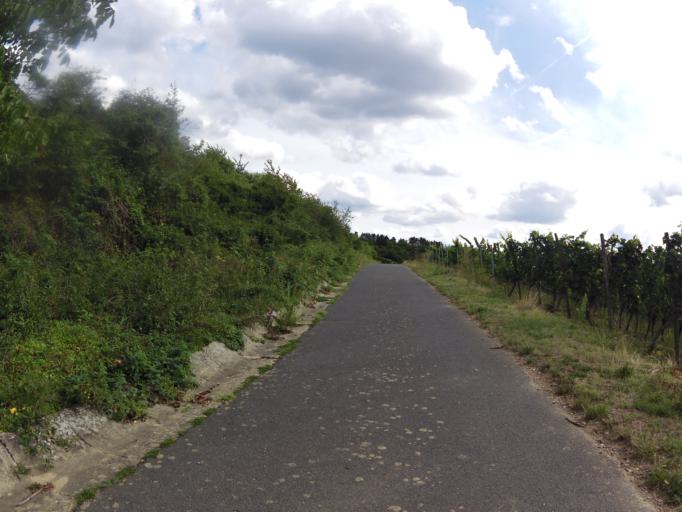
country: DE
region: Bavaria
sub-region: Regierungsbezirk Unterfranken
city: Sommerhausen
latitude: 49.6925
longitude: 10.0334
